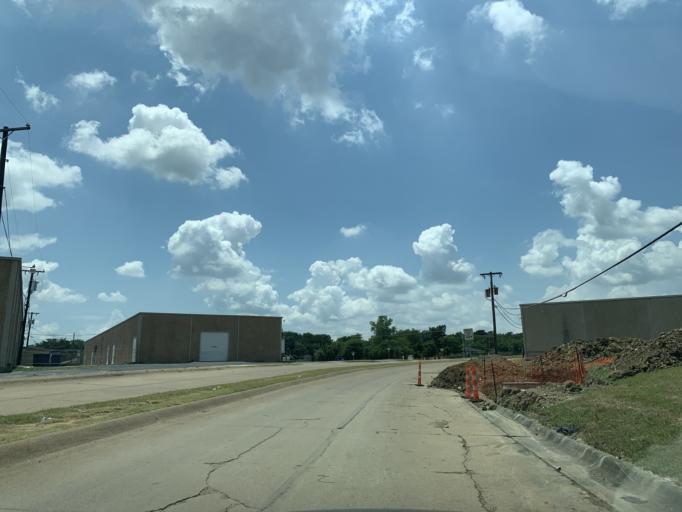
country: US
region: Texas
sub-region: Tarrant County
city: Forest Hill
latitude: 32.7312
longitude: -97.2320
